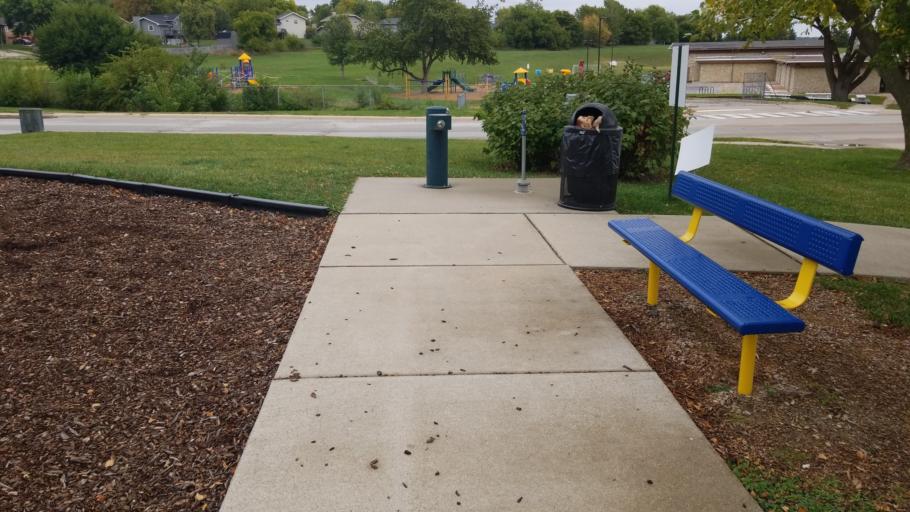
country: US
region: Nebraska
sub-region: Sarpy County
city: Offutt Air Force Base
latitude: 41.1297
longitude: -95.9533
